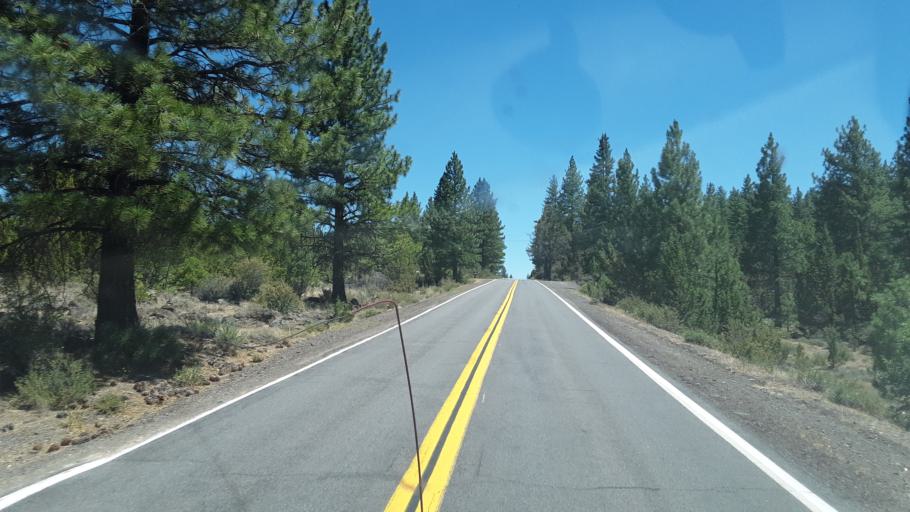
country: US
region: California
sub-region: Lassen County
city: Susanville
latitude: 40.5146
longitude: -120.5771
